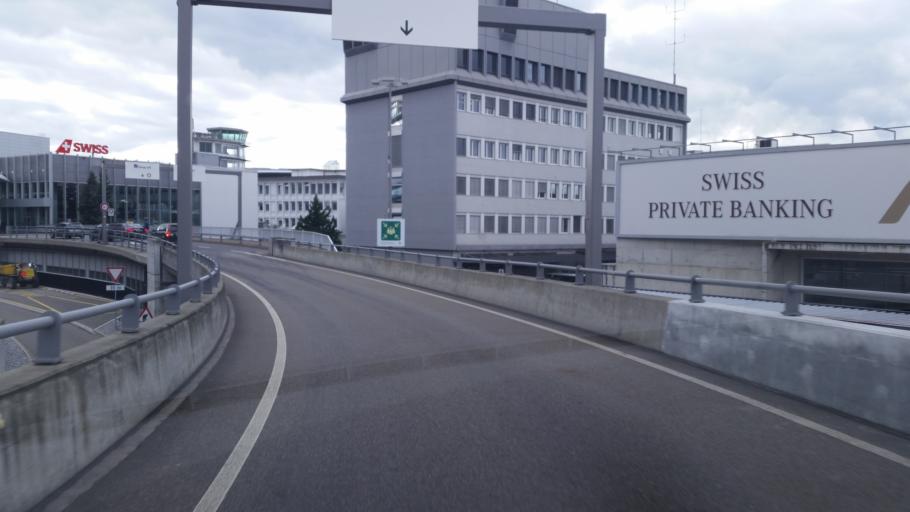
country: CH
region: Zurich
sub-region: Bezirk Buelach
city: Kloten / Holberg
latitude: 47.4532
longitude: 8.5643
